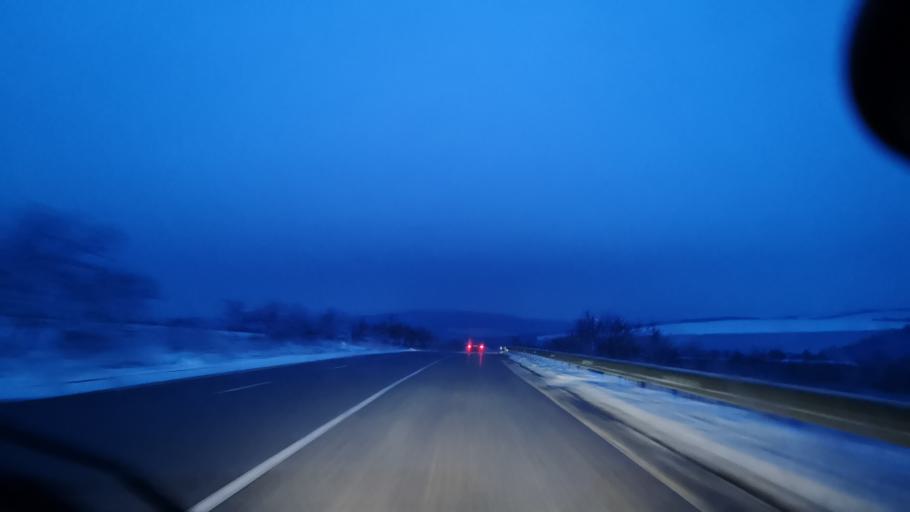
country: MD
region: Orhei
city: Orhei
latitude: 47.5317
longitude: 28.7946
